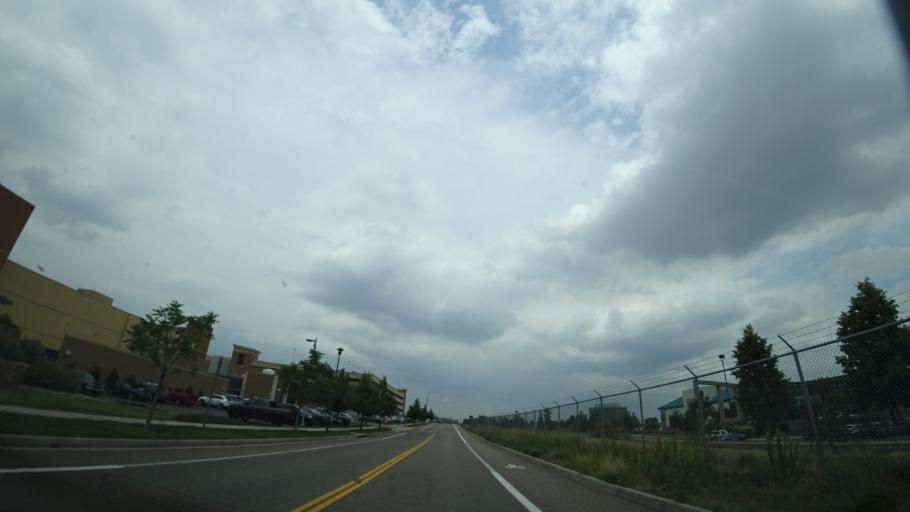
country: US
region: Colorado
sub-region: Jefferson County
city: Lakewood
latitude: 39.7154
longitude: -105.1275
